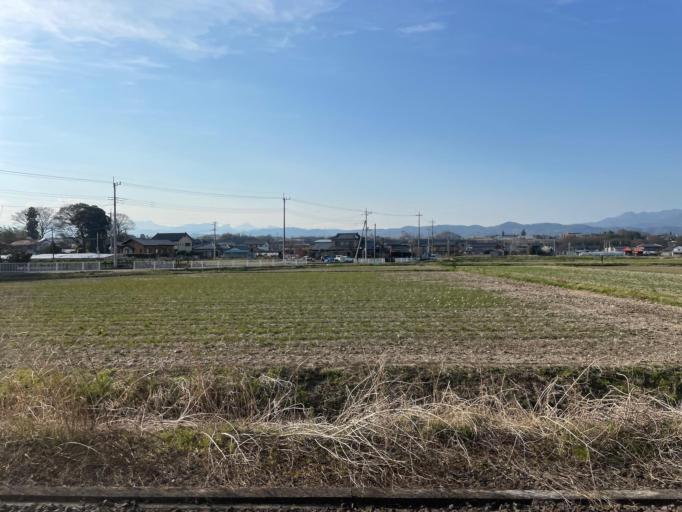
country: JP
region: Gunma
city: Annaka
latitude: 36.3080
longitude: 138.8761
